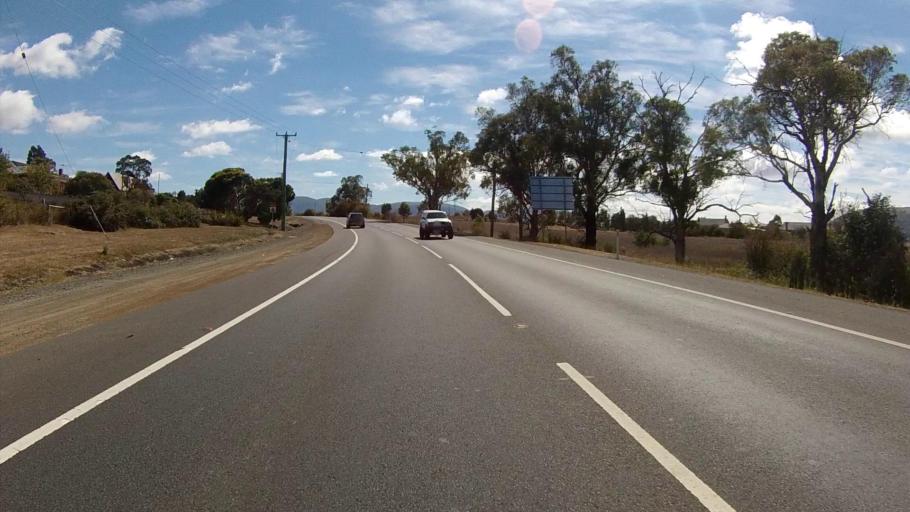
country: AU
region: Tasmania
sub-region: Brighton
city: Bridgewater
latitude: -42.7119
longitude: 147.2445
